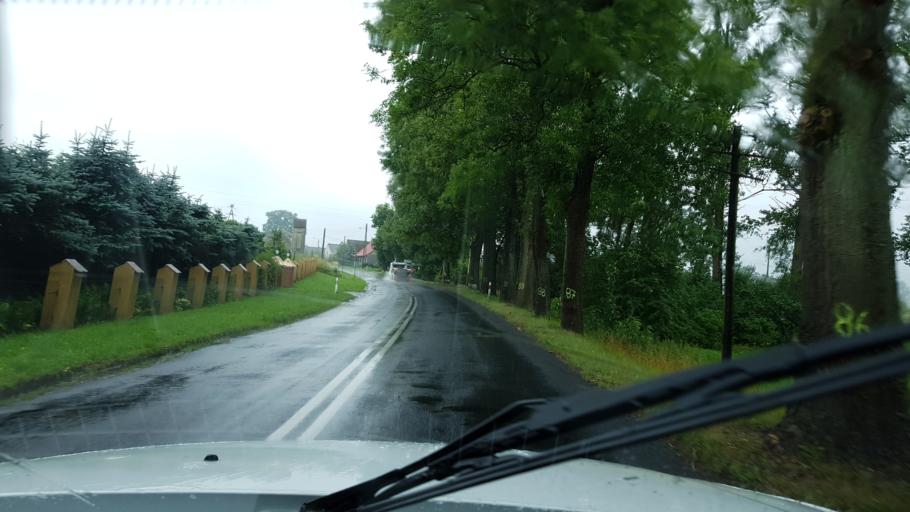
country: PL
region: West Pomeranian Voivodeship
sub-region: Powiat goleniowski
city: Nowogard
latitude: 53.5827
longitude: 15.1386
